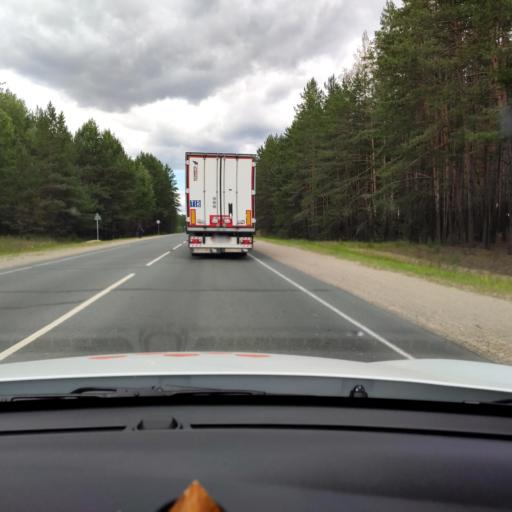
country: RU
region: Mariy-El
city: Krasnogorskiy
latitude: 56.1107
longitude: 48.3450
